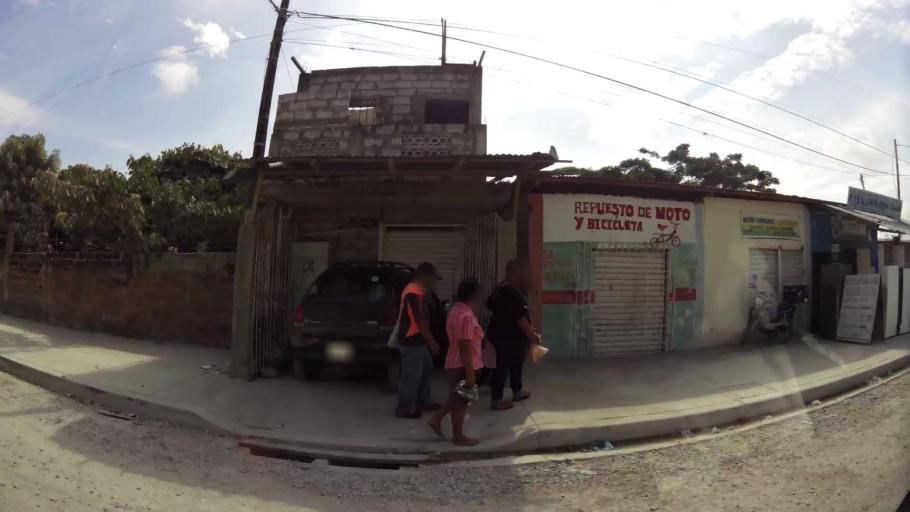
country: EC
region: Guayas
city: Guayaquil
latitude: -2.2708
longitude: -79.8955
